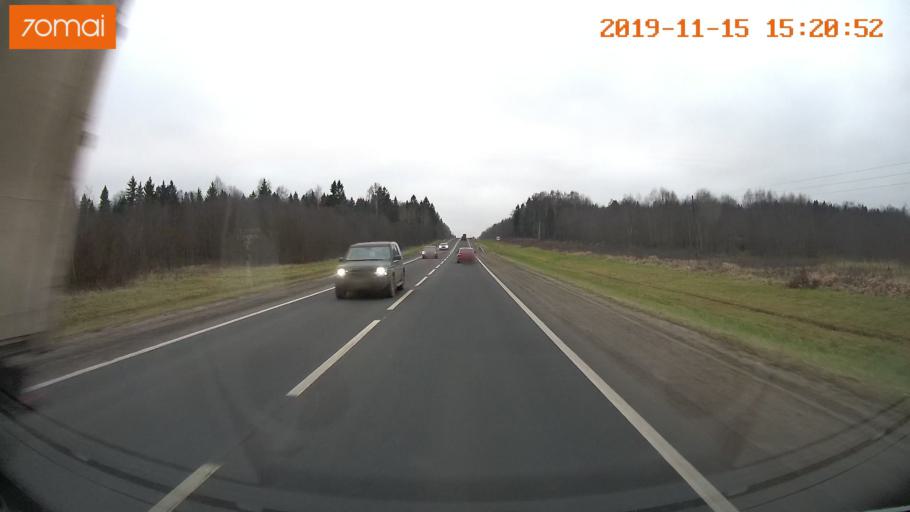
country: RU
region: Jaroslavl
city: Danilov
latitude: 58.2188
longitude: 40.1548
